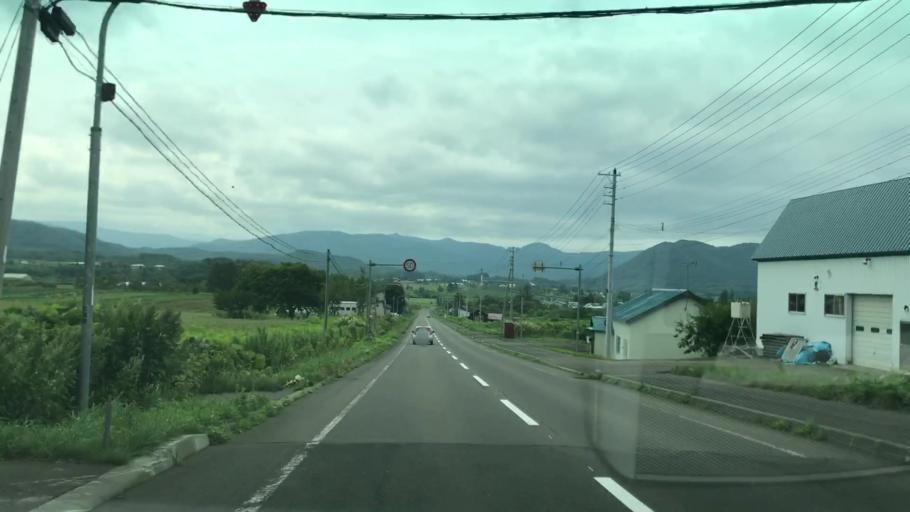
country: JP
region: Hokkaido
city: Yoichi
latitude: 43.1059
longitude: 140.8234
